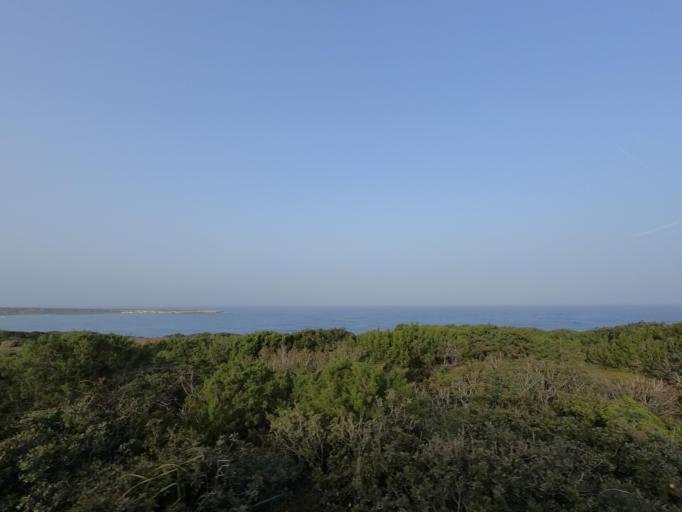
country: CY
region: Pafos
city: Pegeia
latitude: 34.9677
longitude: 32.3135
